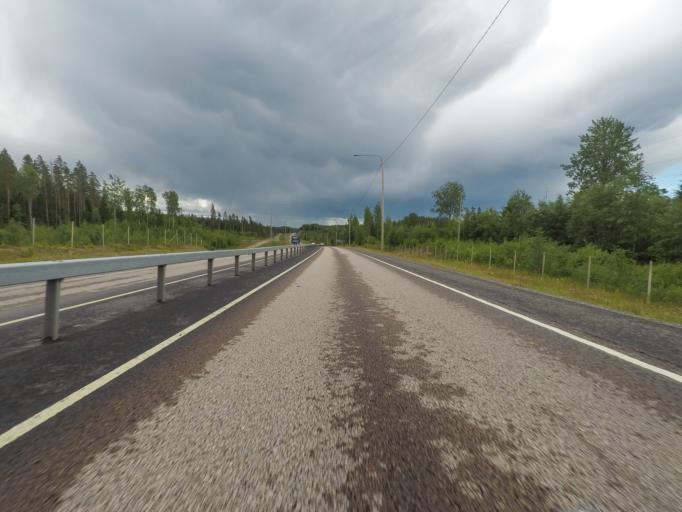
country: FI
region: Central Finland
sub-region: Jyvaeskylae
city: Toivakka
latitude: 62.0137
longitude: 26.0468
